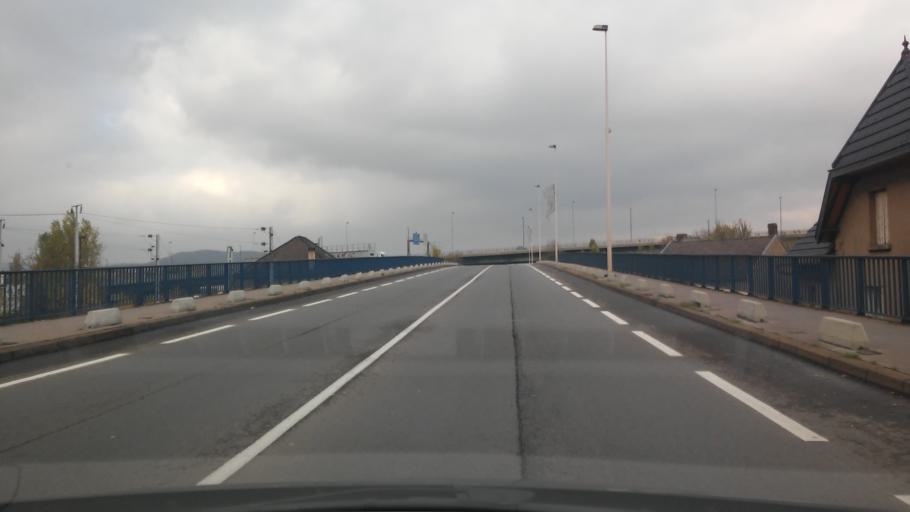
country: FR
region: Lorraine
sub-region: Departement de la Moselle
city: Thionville
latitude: 49.3463
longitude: 6.1610
